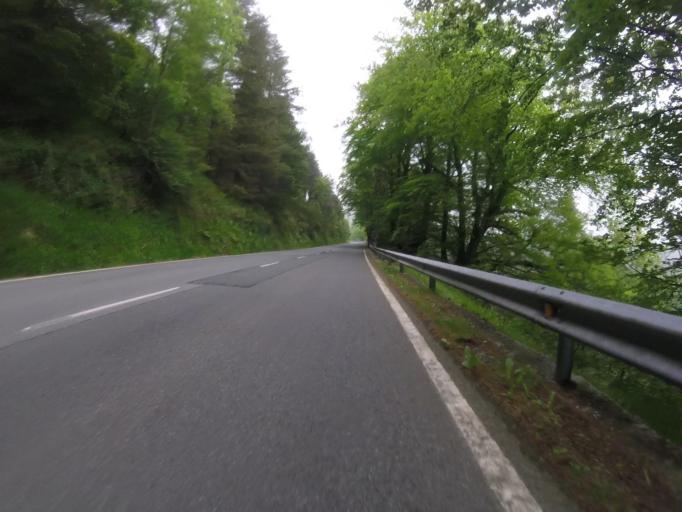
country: ES
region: Navarre
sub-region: Provincia de Navarra
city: Zugarramurdi
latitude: 43.2472
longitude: -1.4828
